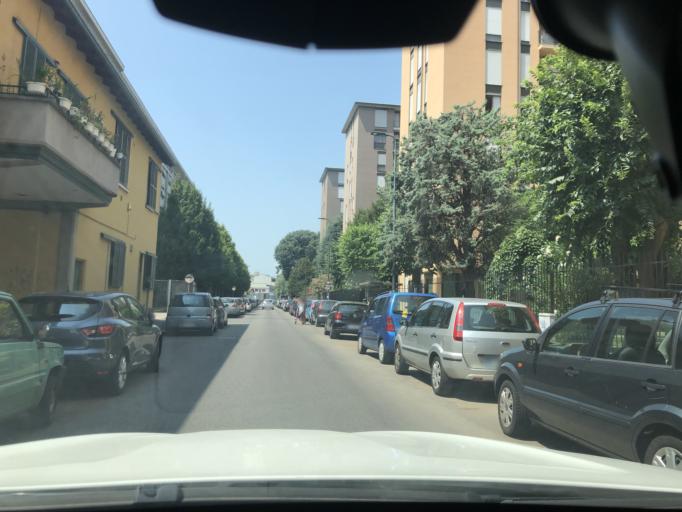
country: IT
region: Lombardy
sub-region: Citta metropolitana di Milano
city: Bresso
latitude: 45.5056
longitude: 9.1729
